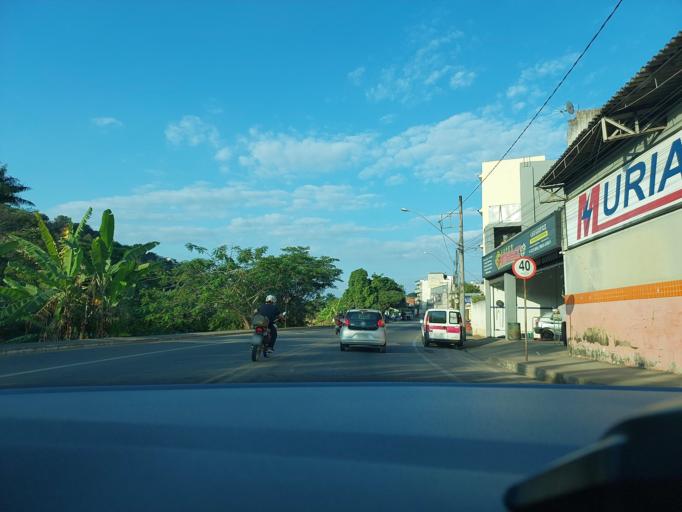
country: BR
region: Minas Gerais
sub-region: Muriae
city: Muriae
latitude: -21.1301
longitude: -42.3931
